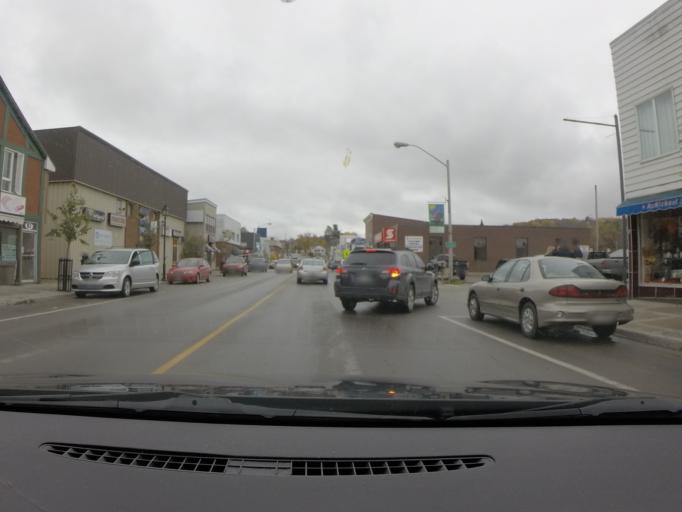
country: CA
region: Ontario
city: Bancroft
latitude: 45.0585
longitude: -77.8545
